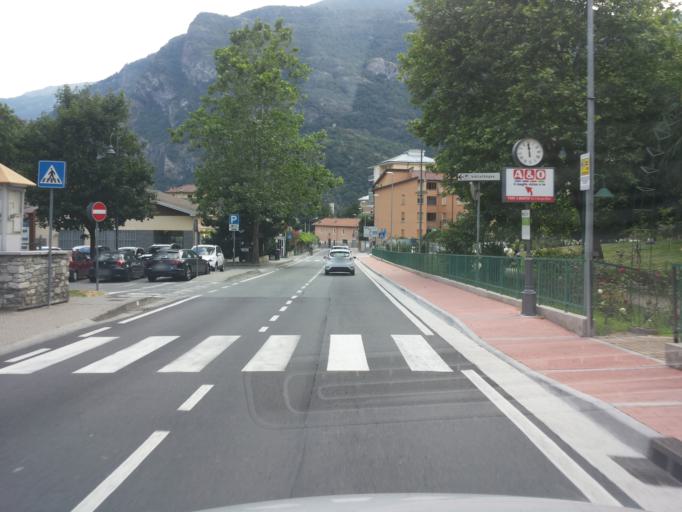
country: IT
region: Aosta Valley
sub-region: Valle d'Aosta
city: Pont-Saint-Martin
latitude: 45.5975
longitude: 7.7995
